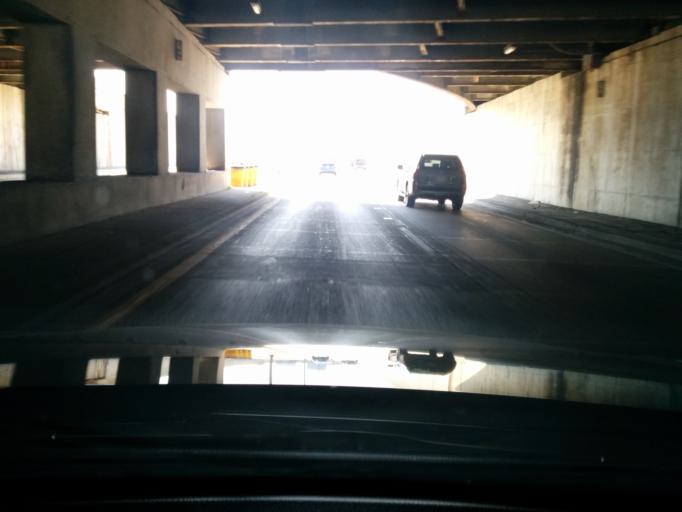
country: US
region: Illinois
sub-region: DuPage County
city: Downers Grove
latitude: 41.8355
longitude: -88.0110
